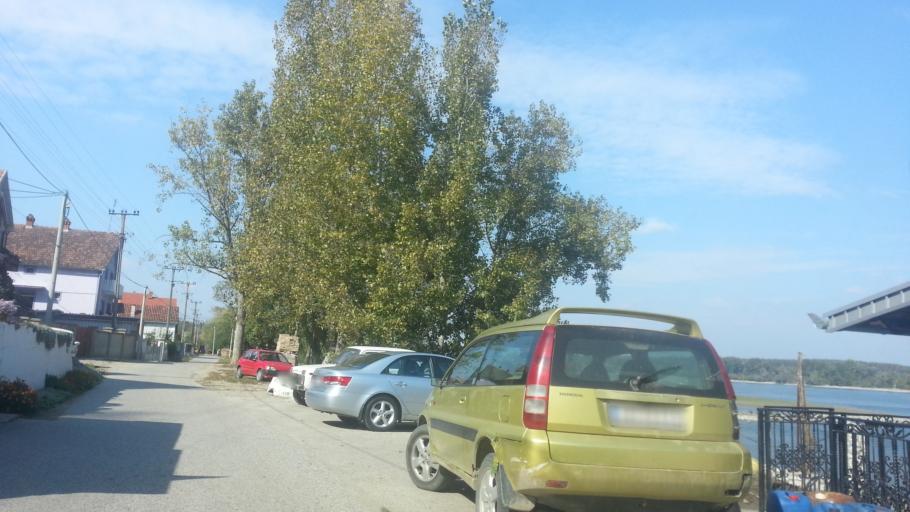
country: RS
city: Novi Slankamen
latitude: 45.1472
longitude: 20.2519
